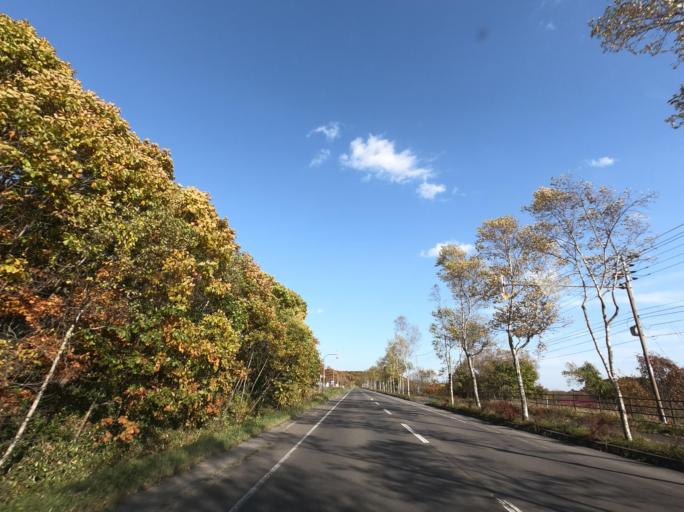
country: JP
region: Hokkaido
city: Kushiro
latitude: 43.0684
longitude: 144.3032
